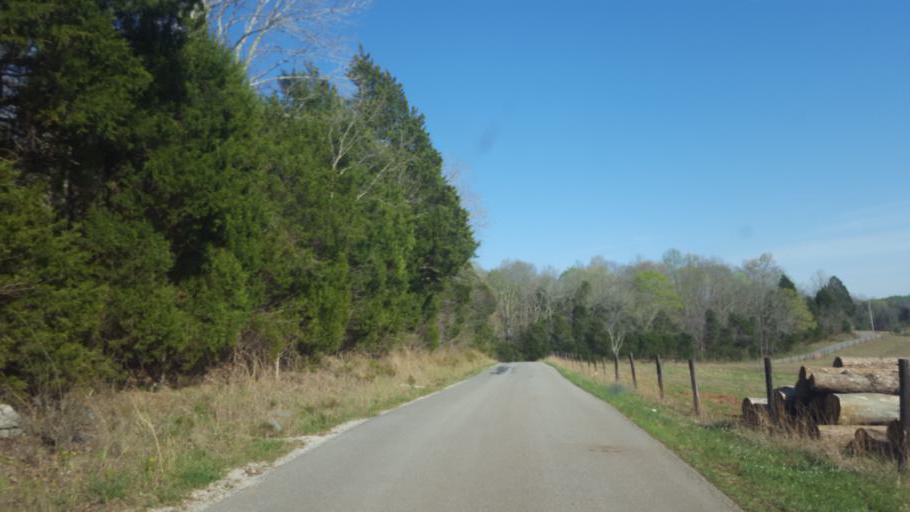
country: US
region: Kentucky
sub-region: Barren County
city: Cave City
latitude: 37.2006
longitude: -86.0169
